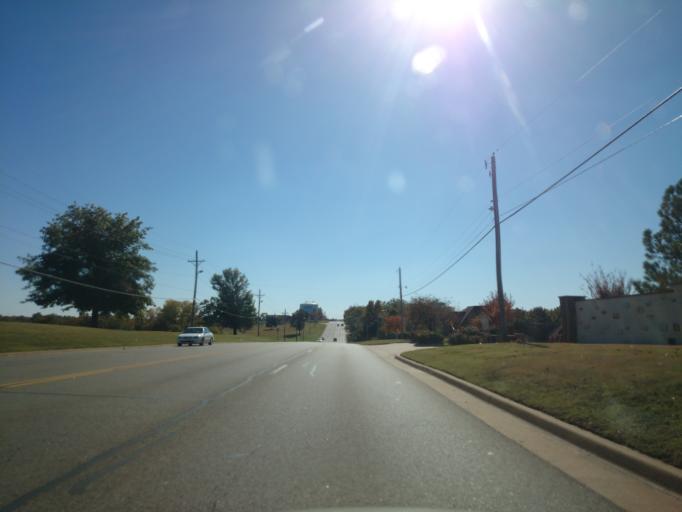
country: US
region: Oklahoma
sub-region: Payne County
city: Stillwater
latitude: 36.1550
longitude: -97.0698
